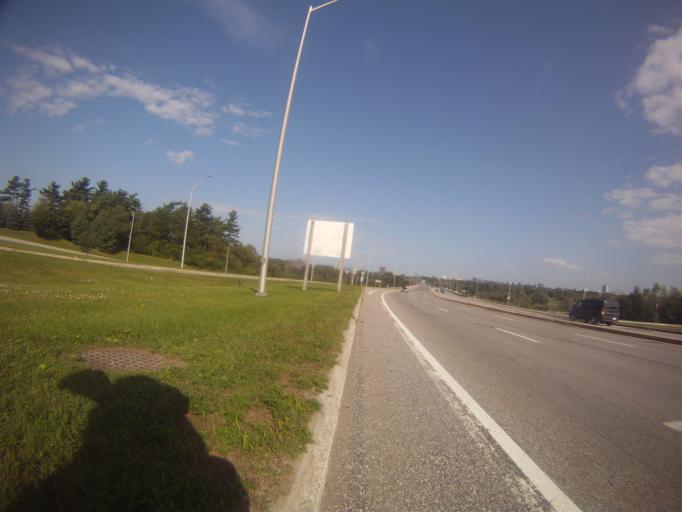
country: CA
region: Ontario
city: Ottawa
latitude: 45.3803
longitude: -75.6847
